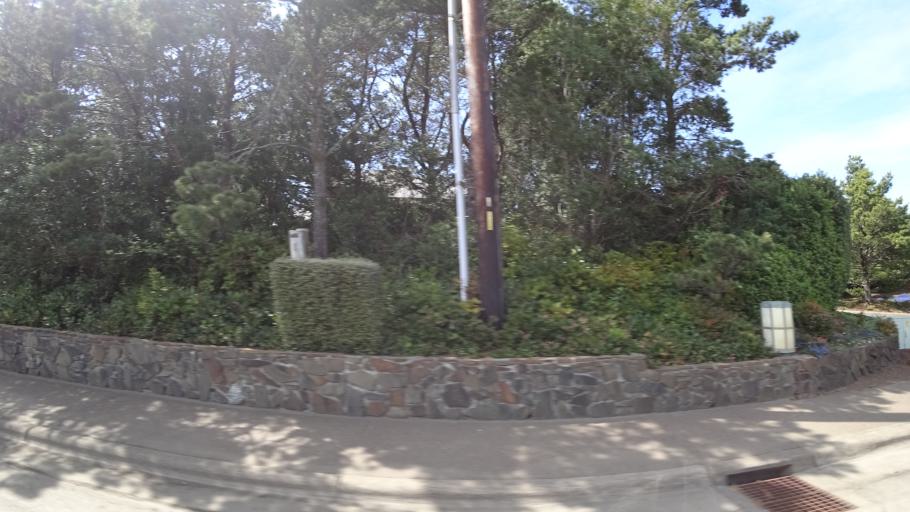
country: US
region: Oregon
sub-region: Lincoln County
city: Lincoln Beach
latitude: 44.8524
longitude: -124.0430
